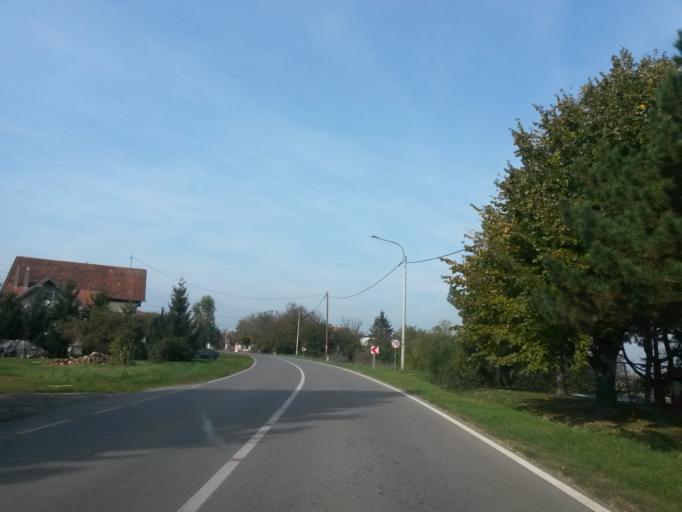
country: HR
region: Osjecko-Baranjska
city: Darda
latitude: 45.6890
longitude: 18.7473
